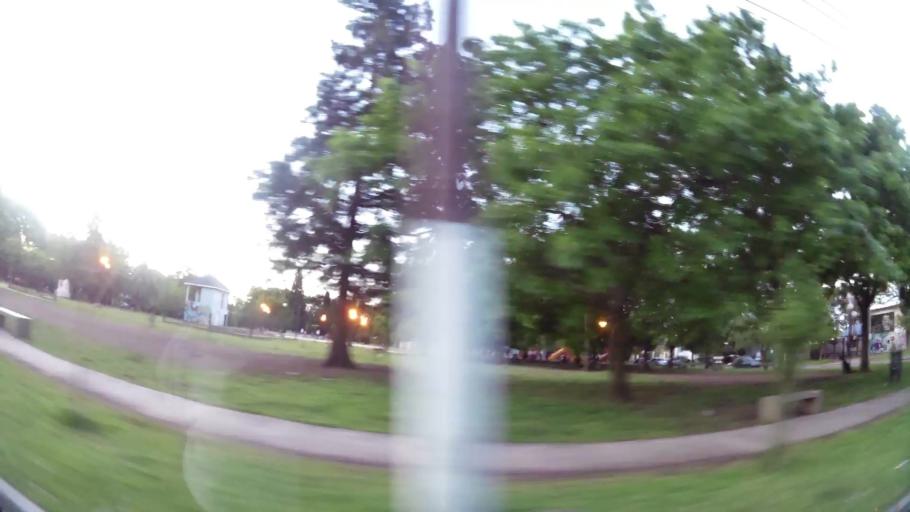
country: AR
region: Buenos Aires
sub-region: Partido de Quilmes
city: Quilmes
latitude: -34.7725
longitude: -58.2059
